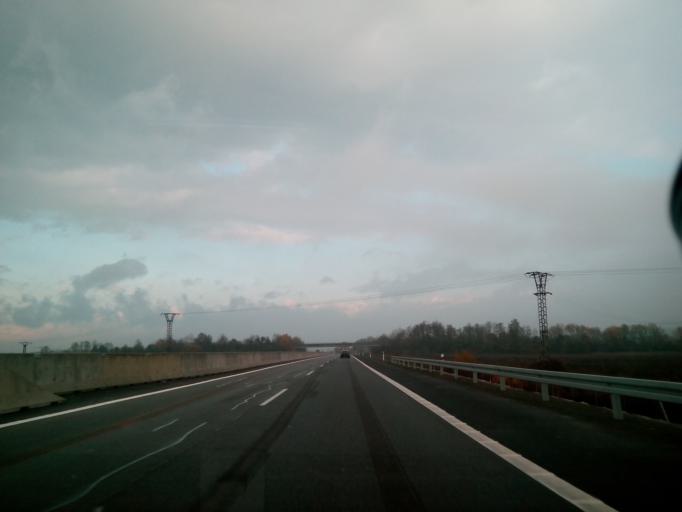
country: SK
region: Kosicky
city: Kosice
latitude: 48.8119
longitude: 21.3097
